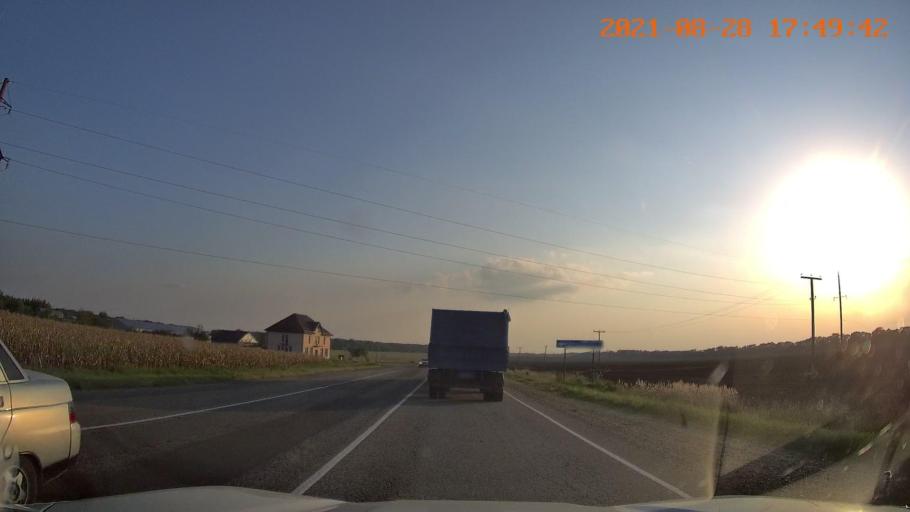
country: RU
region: Krasnodarskiy
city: Konstantinovskaya
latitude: 44.9549
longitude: 40.8264
